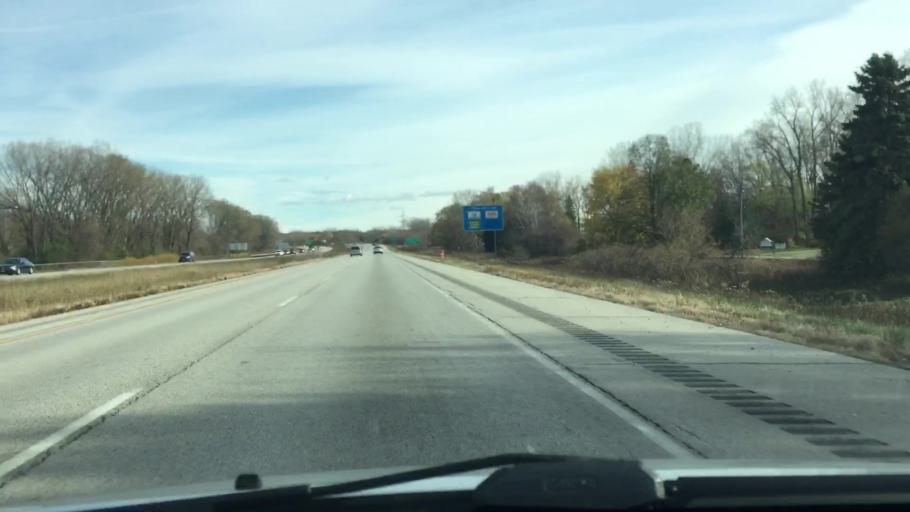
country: US
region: Wisconsin
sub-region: Brown County
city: Green Bay
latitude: 44.5227
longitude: -87.9769
